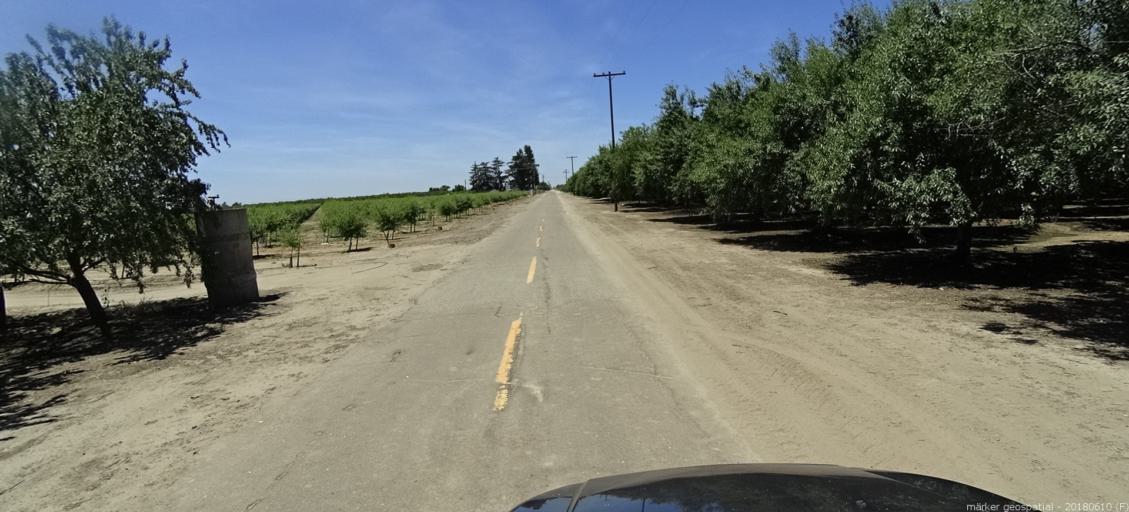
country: US
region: California
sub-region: Madera County
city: Chowchilla
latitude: 37.0473
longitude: -120.2855
